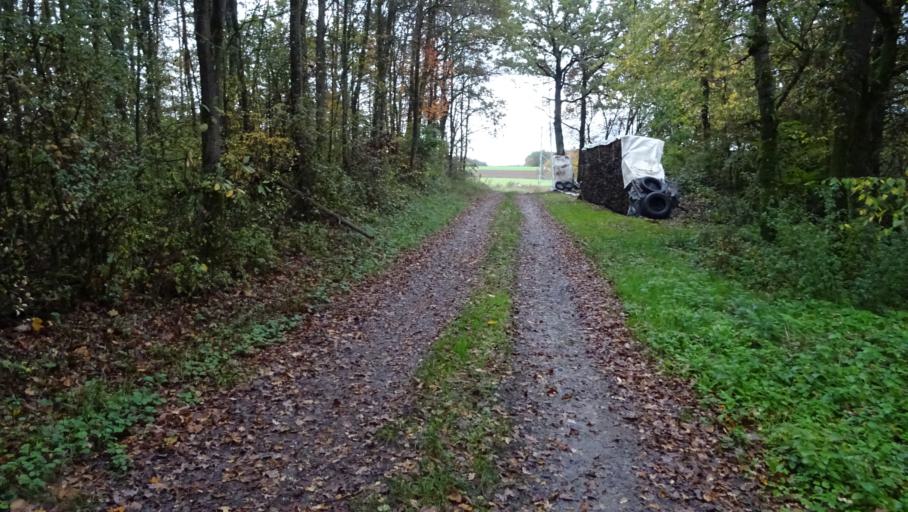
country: DE
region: Baden-Wuerttemberg
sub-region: Karlsruhe Region
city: Billigheim
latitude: 49.3442
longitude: 9.2347
